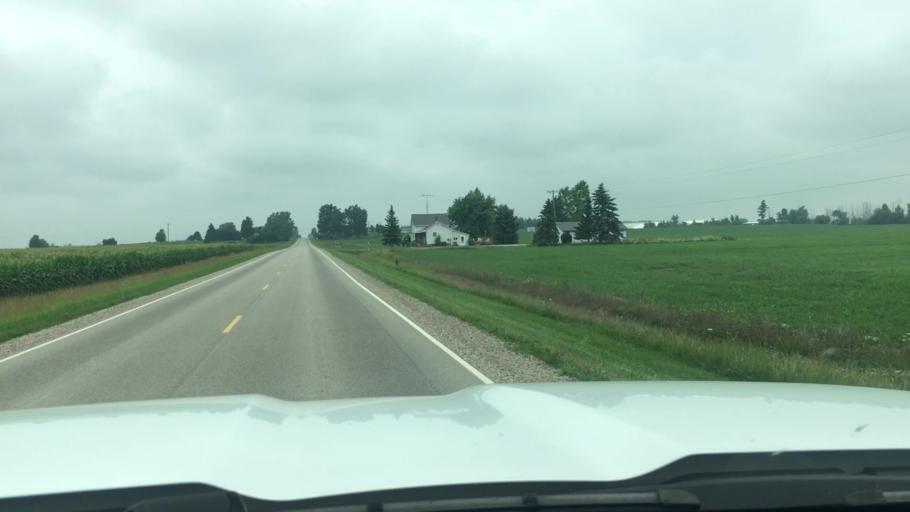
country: US
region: Michigan
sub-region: Sanilac County
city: Brown City
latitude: 43.3039
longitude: -82.9834
